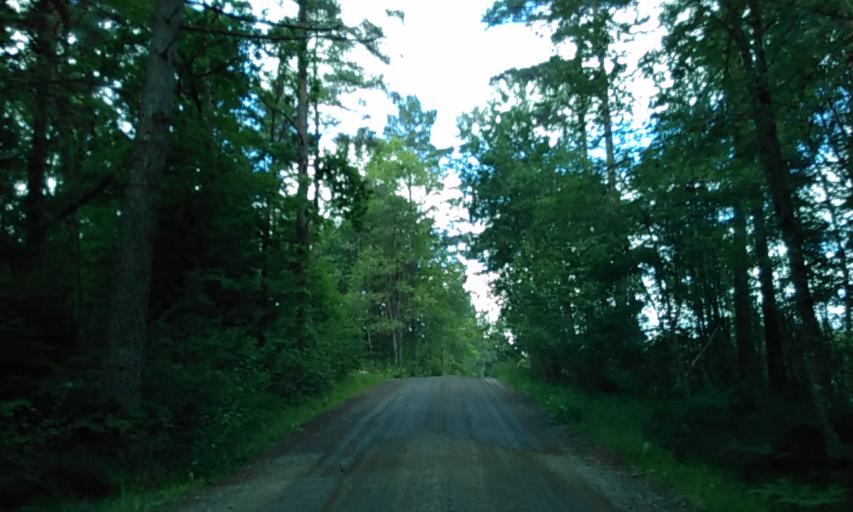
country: SE
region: Vaestra Goetaland
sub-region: Lerums Kommun
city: Grabo
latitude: 57.9087
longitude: 12.3748
